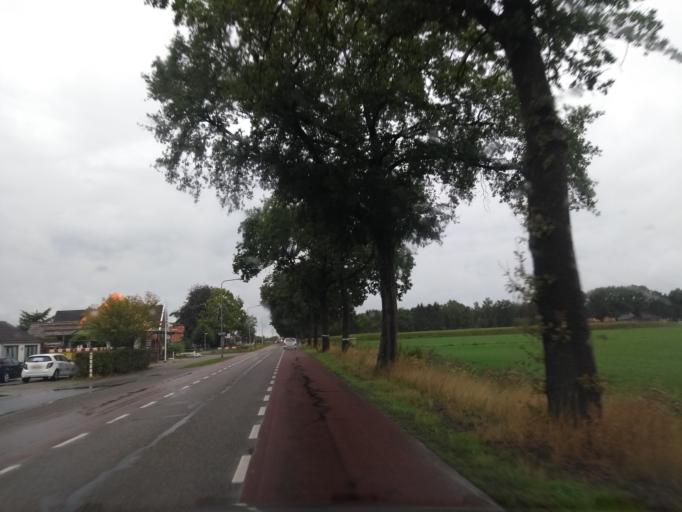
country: NL
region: Overijssel
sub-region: Gemeente Twenterand
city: Vroomshoop
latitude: 52.5036
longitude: 6.5836
